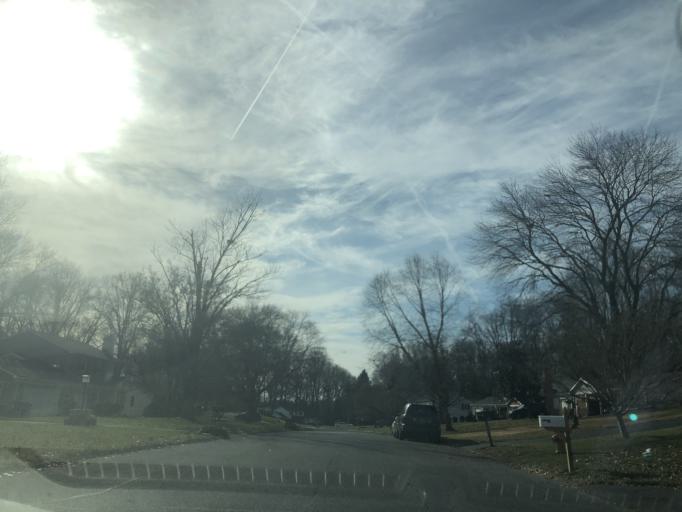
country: US
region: Maryland
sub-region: Howard County
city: Columbia
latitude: 39.2885
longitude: -76.8514
